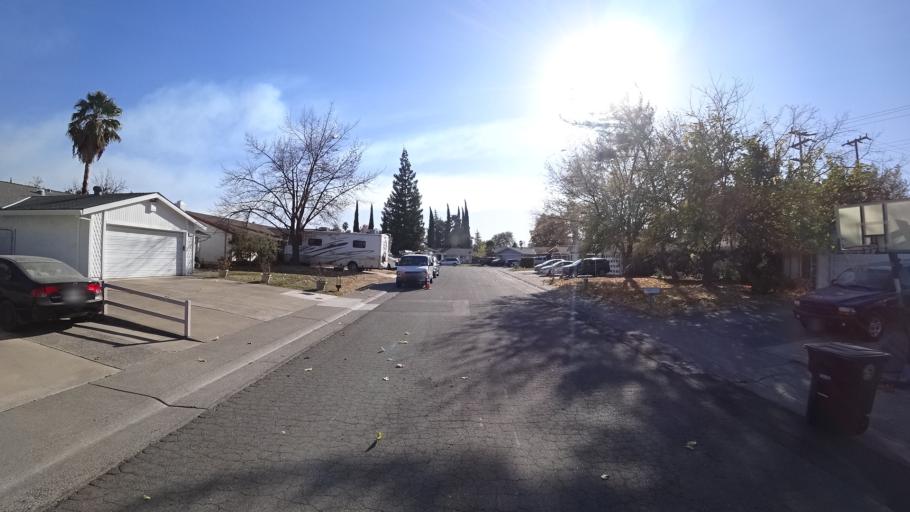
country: US
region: California
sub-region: Sacramento County
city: Antelope
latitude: 38.6972
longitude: -121.3261
